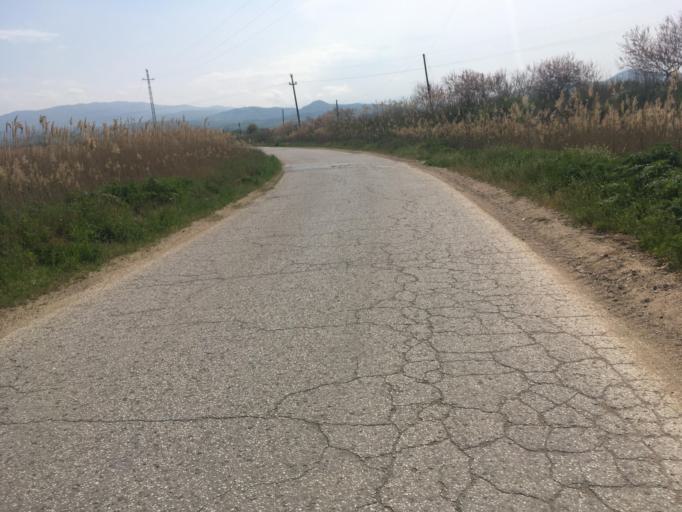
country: MK
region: Karbinci
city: Karbinci
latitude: 41.8011
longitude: 22.2108
